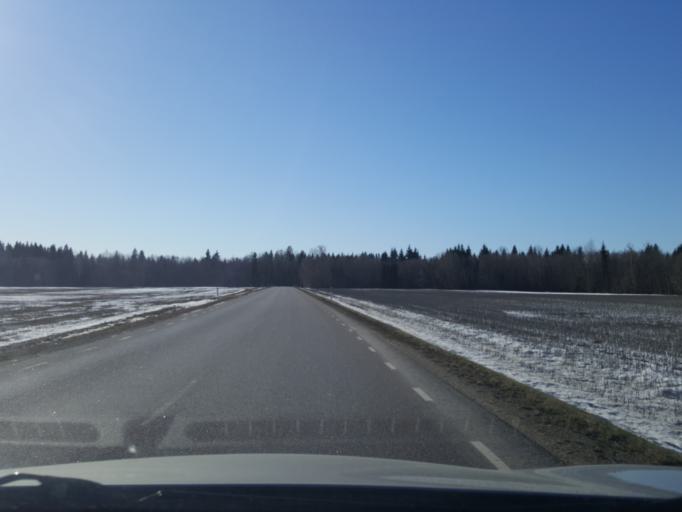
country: EE
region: Viljandimaa
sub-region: Viiratsi vald
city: Viiratsi
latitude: 58.4201
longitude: 25.6778
